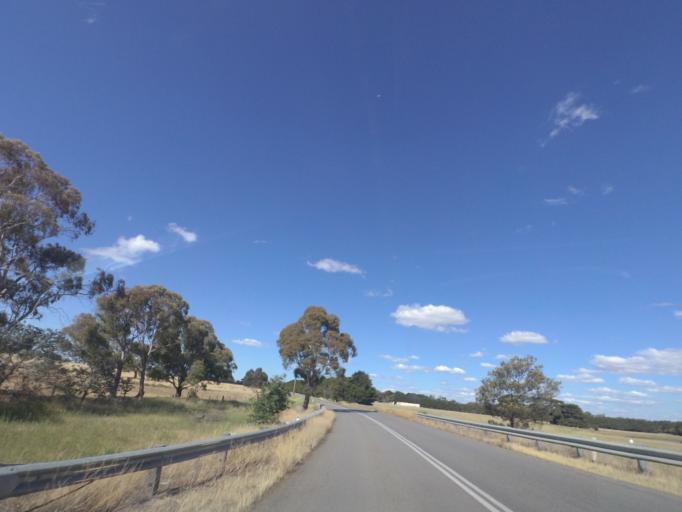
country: AU
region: Victoria
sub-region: Hume
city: Sunbury
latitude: -37.4396
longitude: 144.8344
